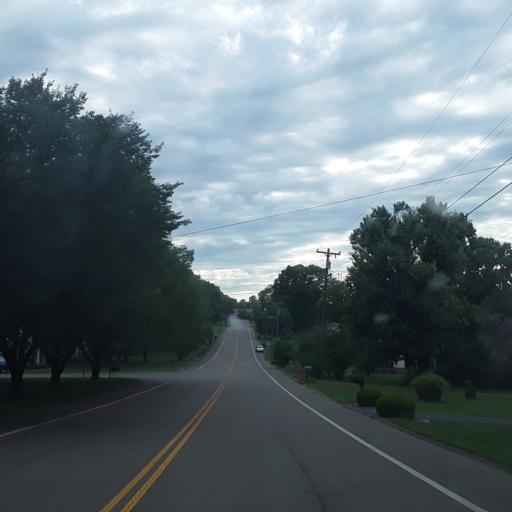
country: US
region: Tennessee
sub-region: Wilson County
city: Green Hill
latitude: 36.1664
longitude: -86.5879
